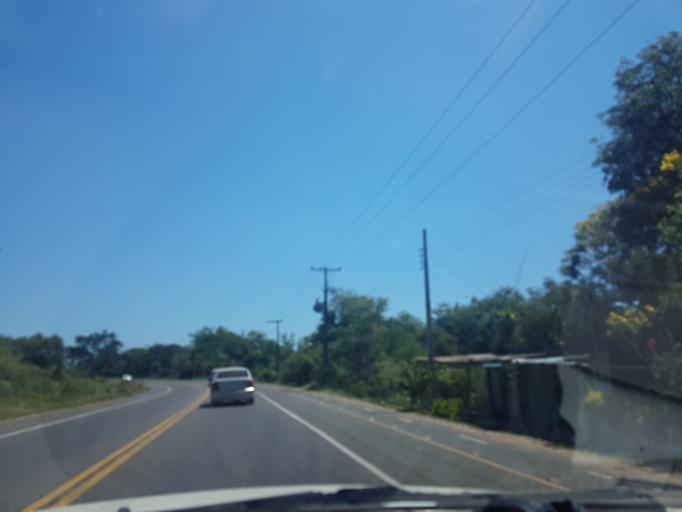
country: PY
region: Central
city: Limpio
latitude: -25.2174
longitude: -57.4170
